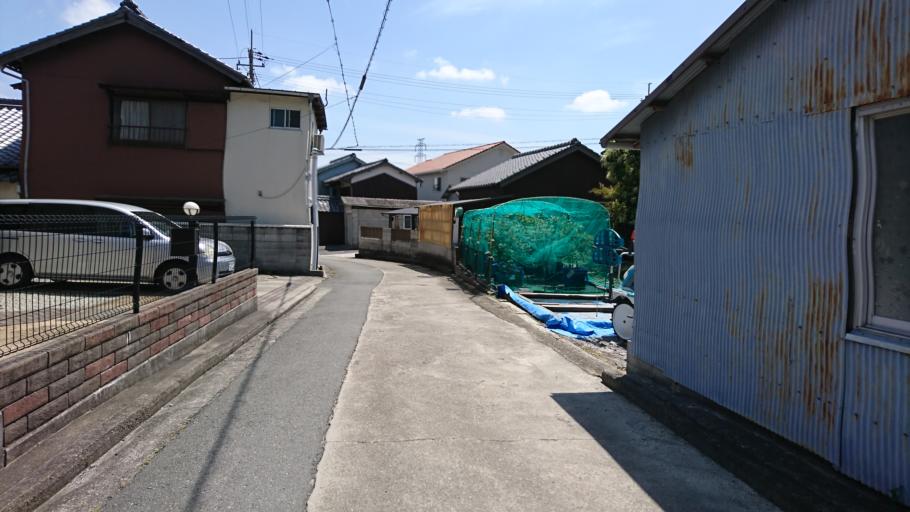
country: JP
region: Hyogo
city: Kakogawacho-honmachi
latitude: 34.8075
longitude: 134.7901
